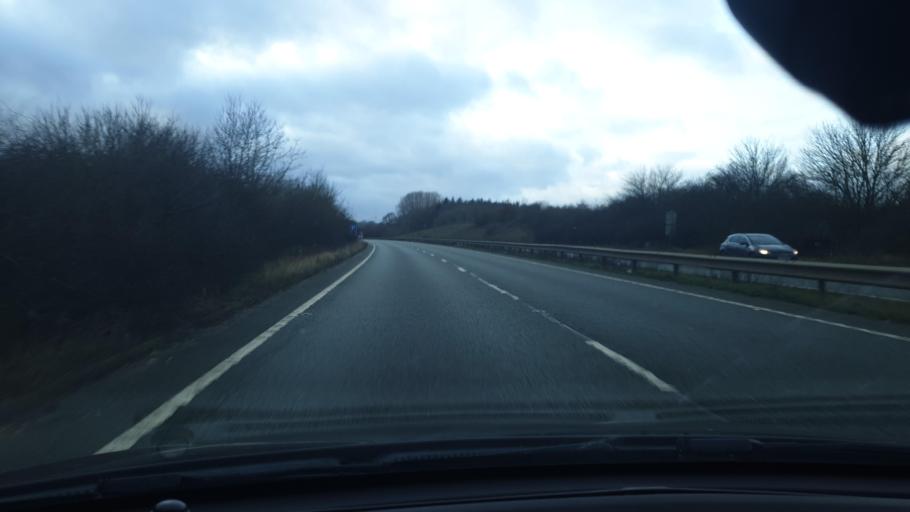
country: GB
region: England
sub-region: Northamptonshire
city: Desborough
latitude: 52.4052
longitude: -0.8867
